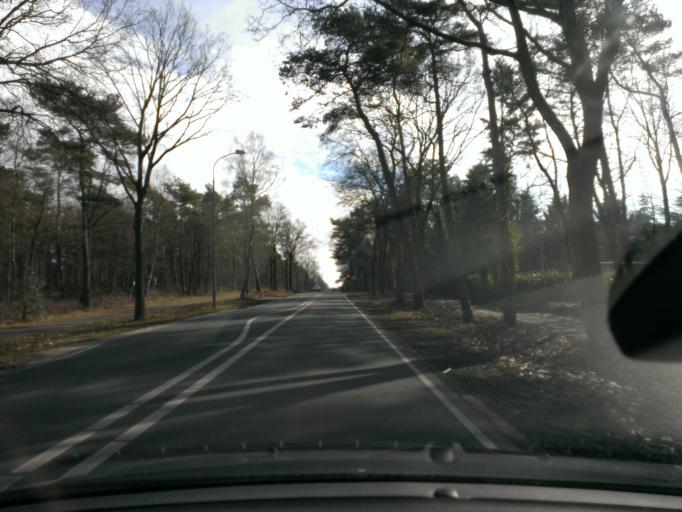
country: NL
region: Gelderland
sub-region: Gemeente Hattem
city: Hattem
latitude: 52.4500
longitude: 6.0059
